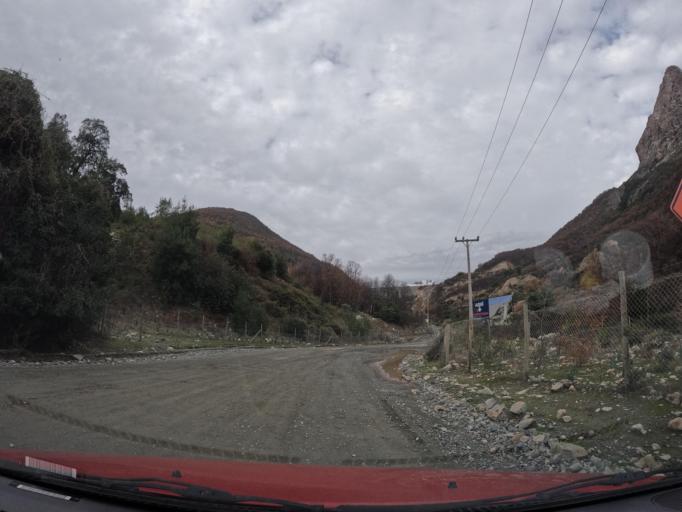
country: CL
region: Maule
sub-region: Provincia de Linares
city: Colbun
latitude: -35.8547
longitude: -71.1934
